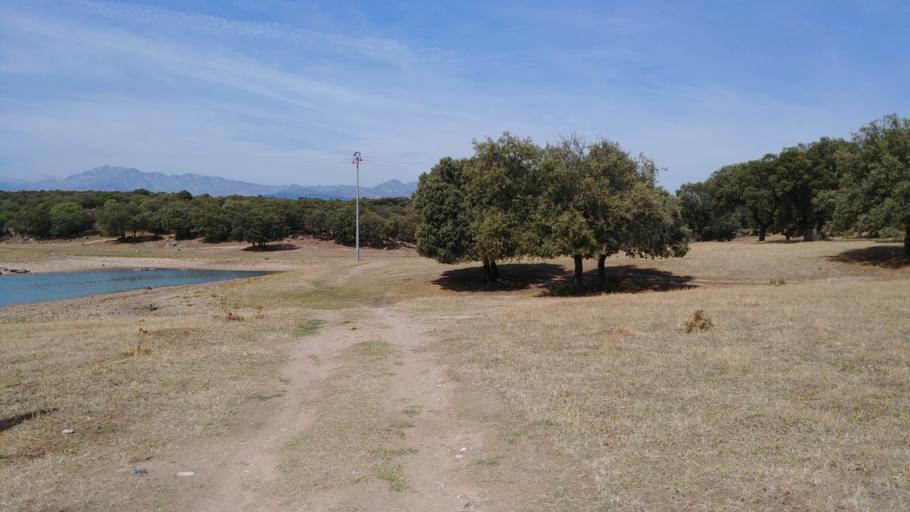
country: ES
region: Castille-La Mancha
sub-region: Province of Toledo
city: Navalcan
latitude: 40.0499
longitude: -5.1266
